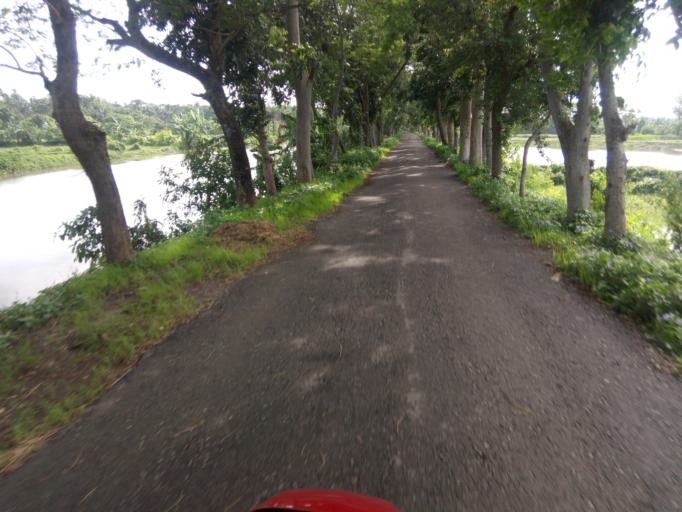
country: BD
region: Khulna
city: Bhatpara Abhaynagar
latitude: 22.9495
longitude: 89.5457
